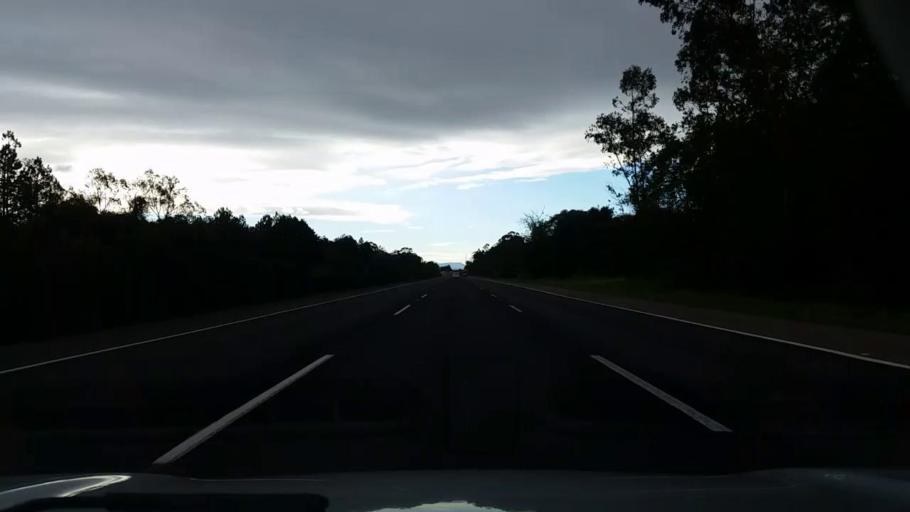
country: BR
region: Rio Grande do Sul
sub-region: Taquara
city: Taquara
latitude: -29.8902
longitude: -50.7013
